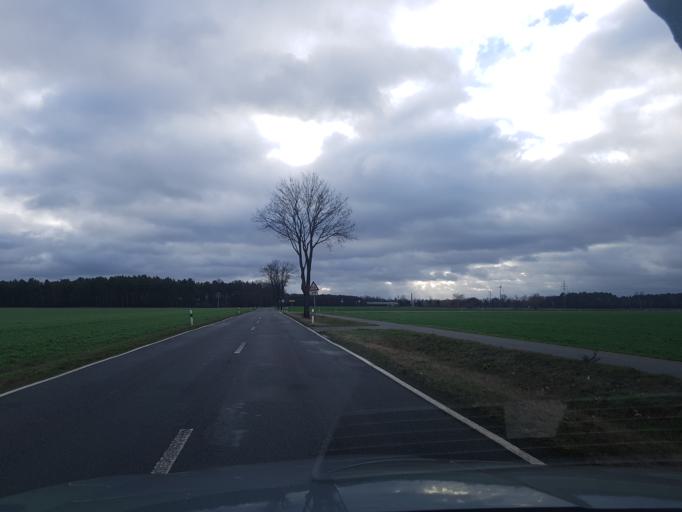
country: DE
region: Brandenburg
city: Herzberg
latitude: 51.6698
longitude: 13.2320
